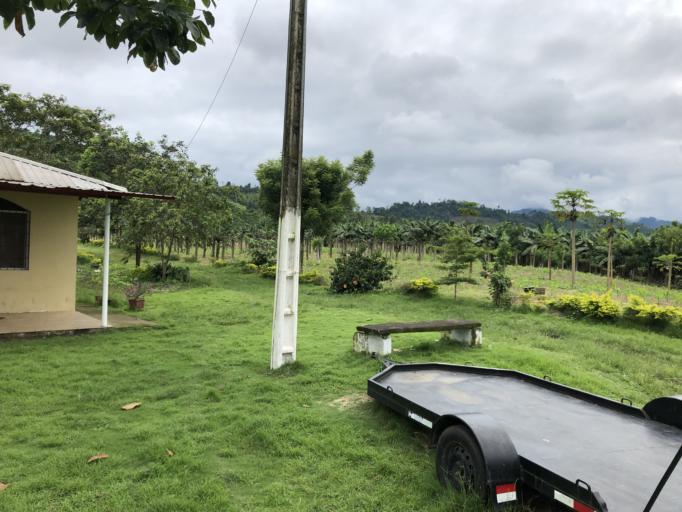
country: EC
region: Cotopaxi
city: La Mana
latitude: -0.9597
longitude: -79.2492
